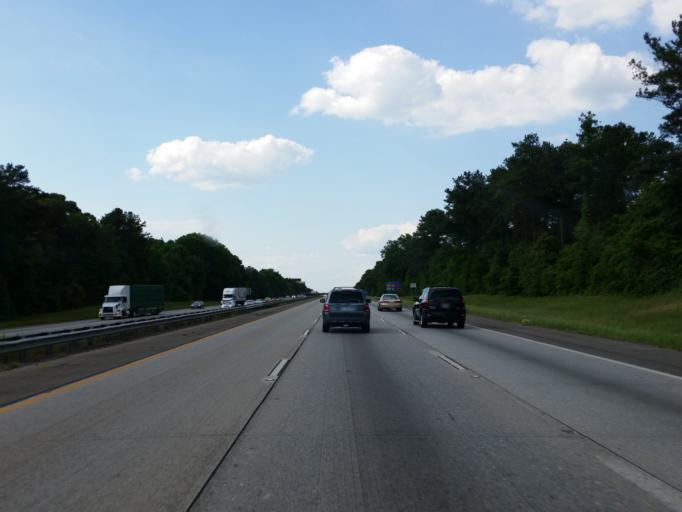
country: US
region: Georgia
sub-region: Peach County
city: Byron
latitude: 32.6355
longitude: -83.7434
